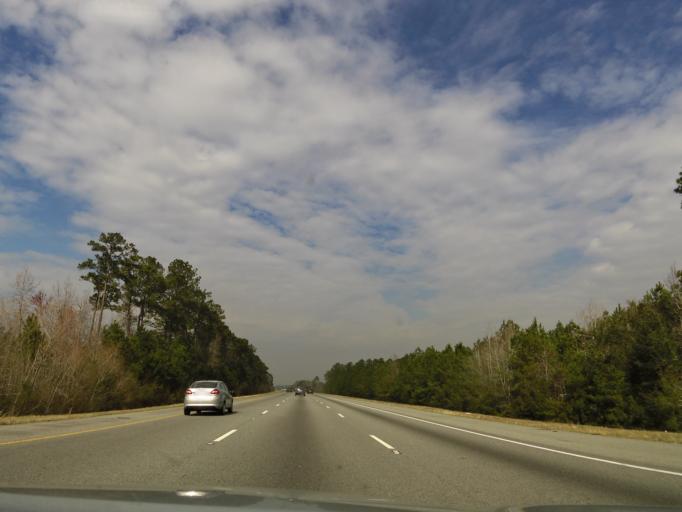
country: US
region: Georgia
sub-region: Liberty County
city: Midway
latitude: 31.7459
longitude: -81.3847
